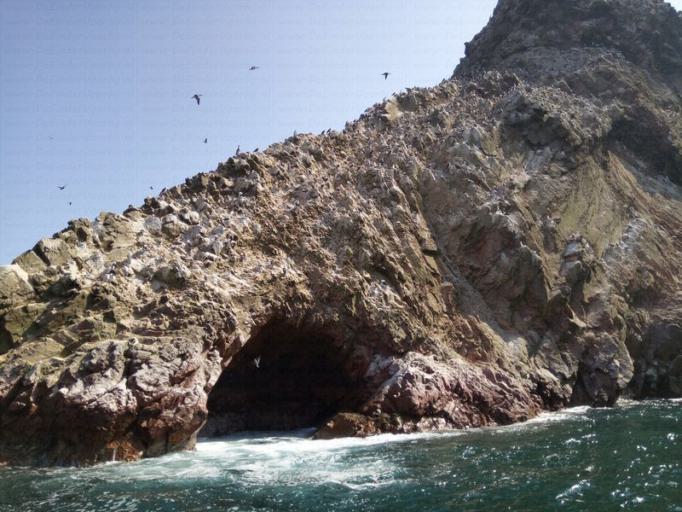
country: PE
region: Ica
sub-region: Provincia de Pisco
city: Paracas
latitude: -13.7375
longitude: -76.3973
